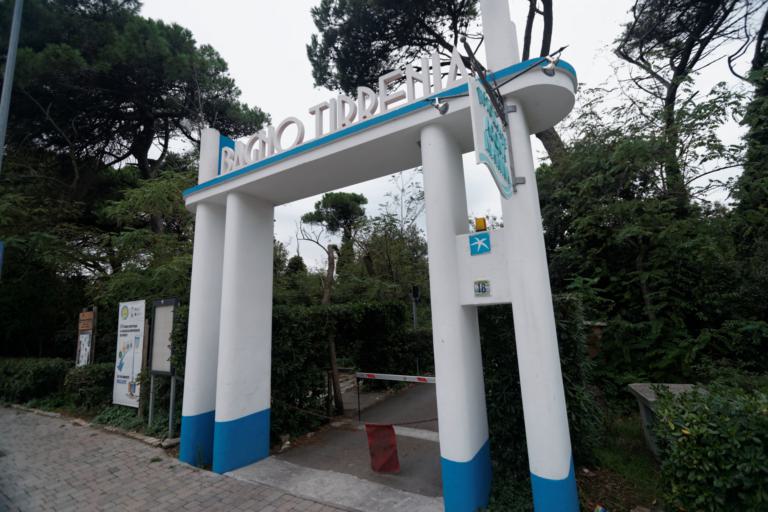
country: IT
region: Tuscany
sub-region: Province of Pisa
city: Marina di Pisa-Tirrenia-Calambrone
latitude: 43.6301
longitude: 10.2916
